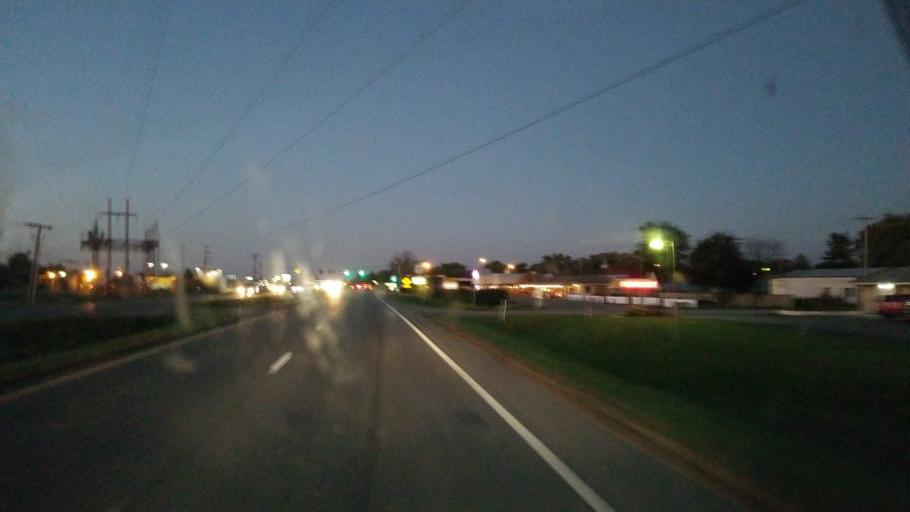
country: US
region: Ohio
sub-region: Pickaway County
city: Logan Elm Village
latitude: 39.5649
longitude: -82.9556
